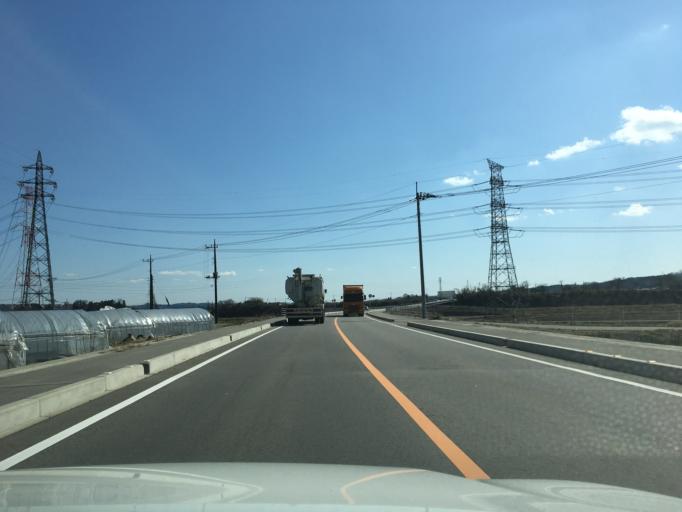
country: JP
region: Tochigi
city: Otawara
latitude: 36.7892
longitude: 140.1162
